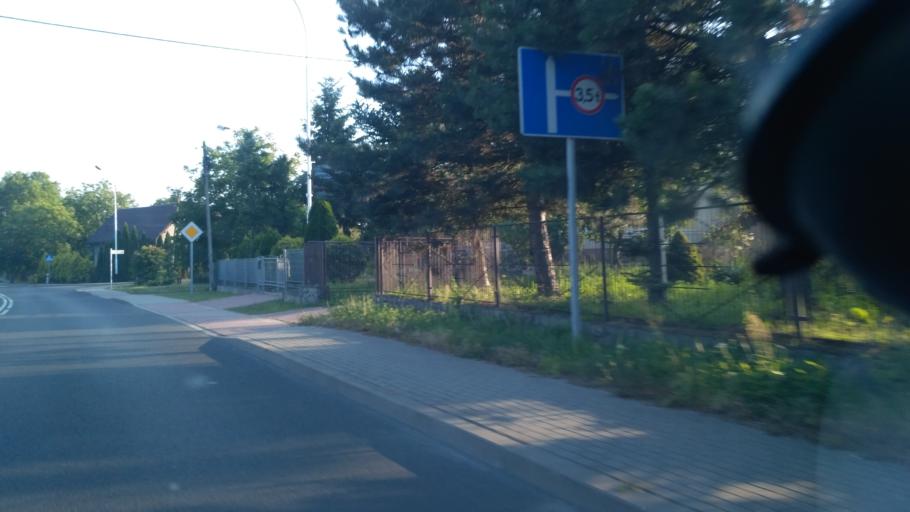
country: PL
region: Subcarpathian Voivodeship
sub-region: Powiat lezajski
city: Lezajsk
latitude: 50.2697
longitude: 22.4240
